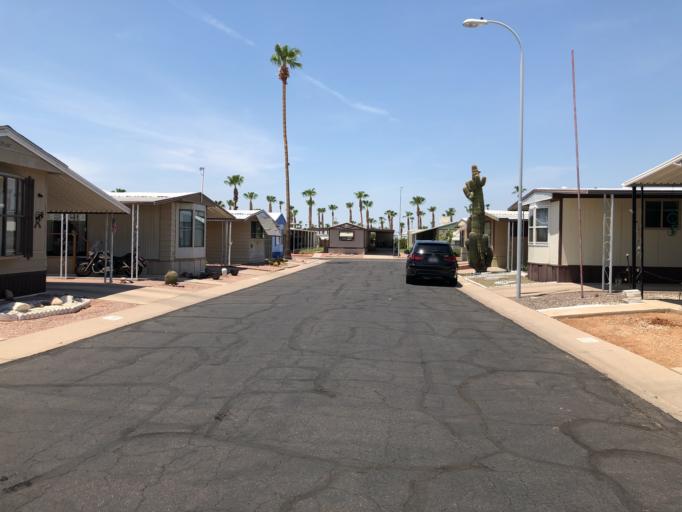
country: US
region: Arizona
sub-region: Maricopa County
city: Mesa
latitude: 33.4206
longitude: -111.7456
